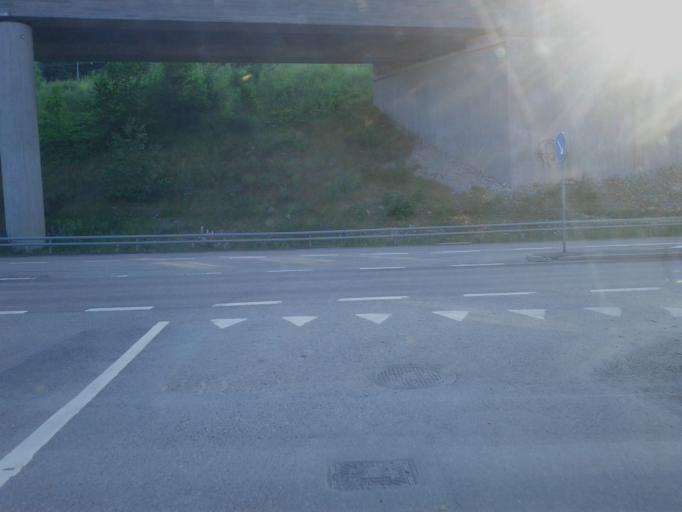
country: SE
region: Vaesternorrland
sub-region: OErnskoeldsviks Kommun
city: Ornskoldsvik
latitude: 63.2841
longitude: 18.7085
